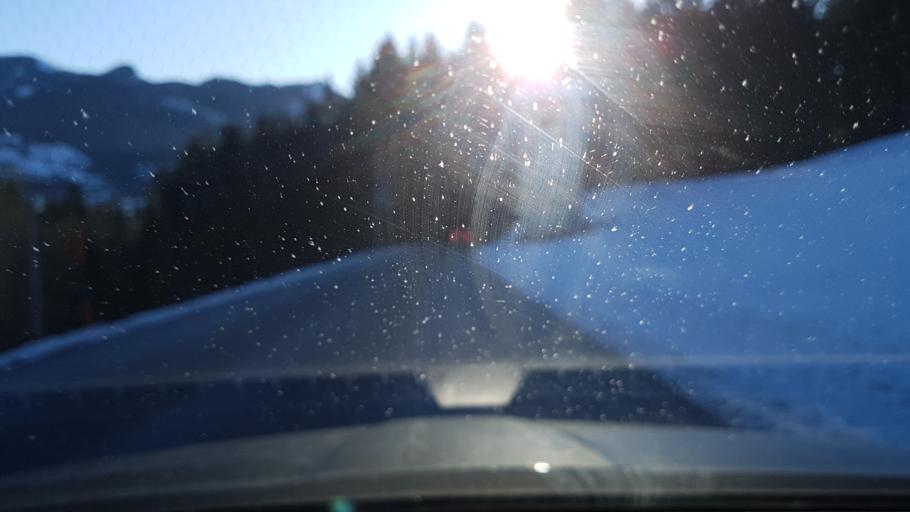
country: AT
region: Salzburg
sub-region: Politischer Bezirk Hallein
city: Scheffau am Tennengebirge
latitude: 47.6510
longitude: 13.2071
